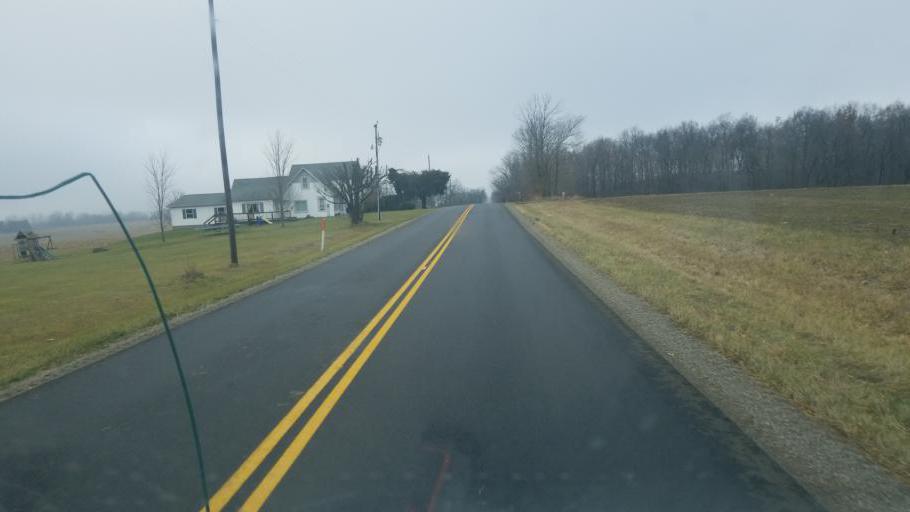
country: US
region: Ohio
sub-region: Champaign County
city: North Lewisburg
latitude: 40.2810
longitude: -83.5700
